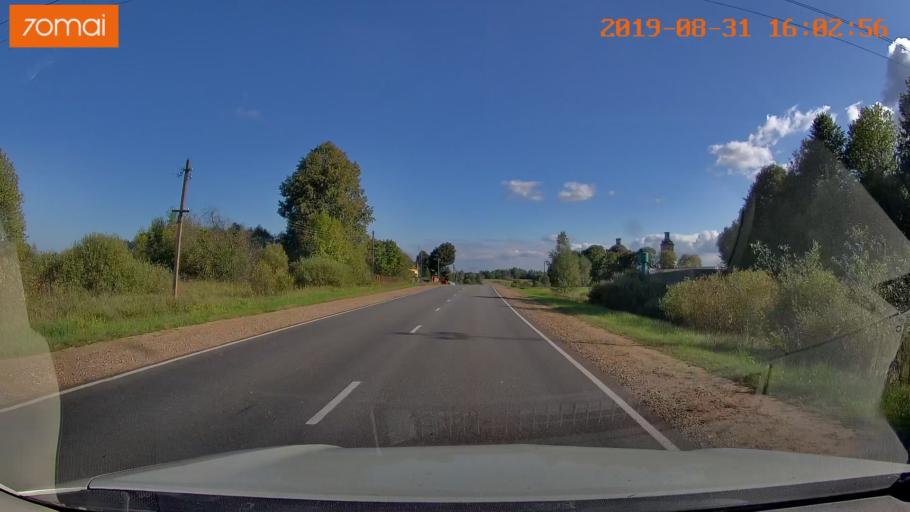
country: RU
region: Kaluga
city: Yukhnov
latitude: 54.6700
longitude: 35.3083
